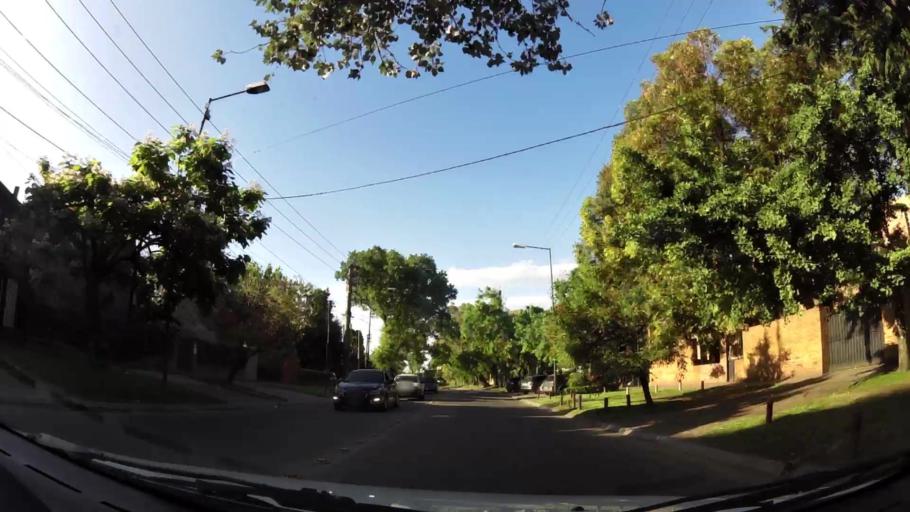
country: AR
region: Buenos Aires
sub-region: Partido de San Isidro
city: San Isidro
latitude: -34.4778
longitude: -58.5552
